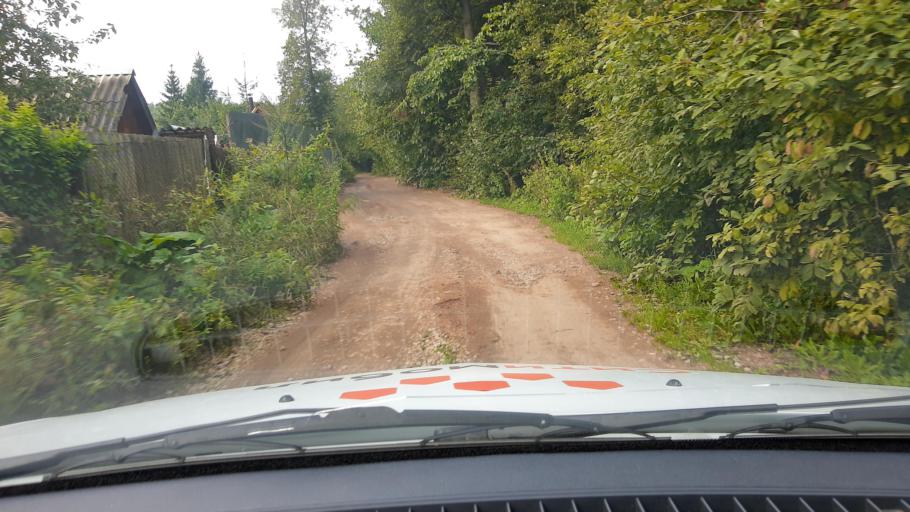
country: RU
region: Bashkortostan
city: Kabakovo
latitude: 54.7100
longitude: 56.1390
